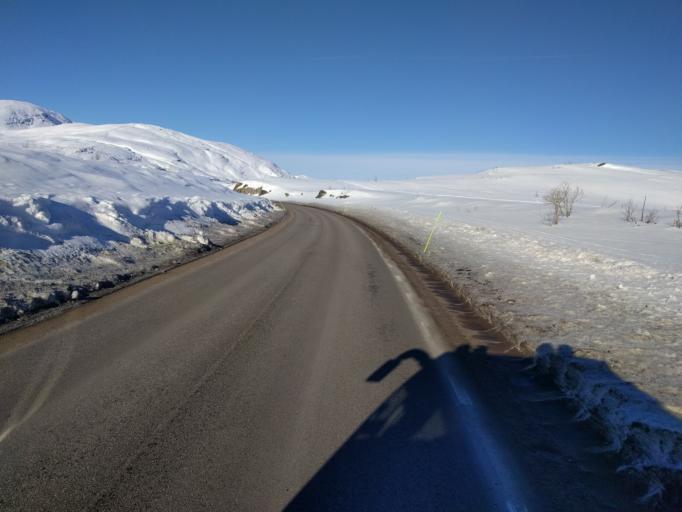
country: NO
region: Troms
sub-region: Bardu
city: Setermoen
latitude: 68.4308
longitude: 18.2022
